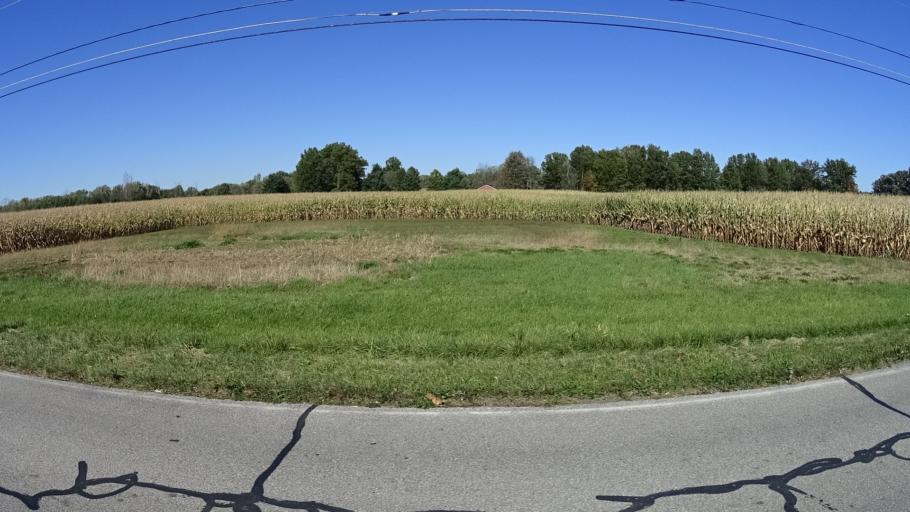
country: US
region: Ohio
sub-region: Lorain County
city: Oberlin
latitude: 41.2793
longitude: -82.1942
